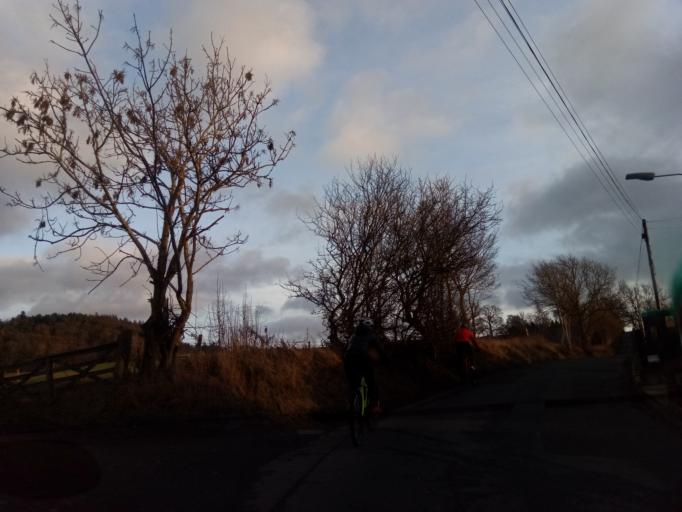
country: GB
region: Scotland
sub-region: The Scottish Borders
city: Selkirk
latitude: 55.5725
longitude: -2.8162
